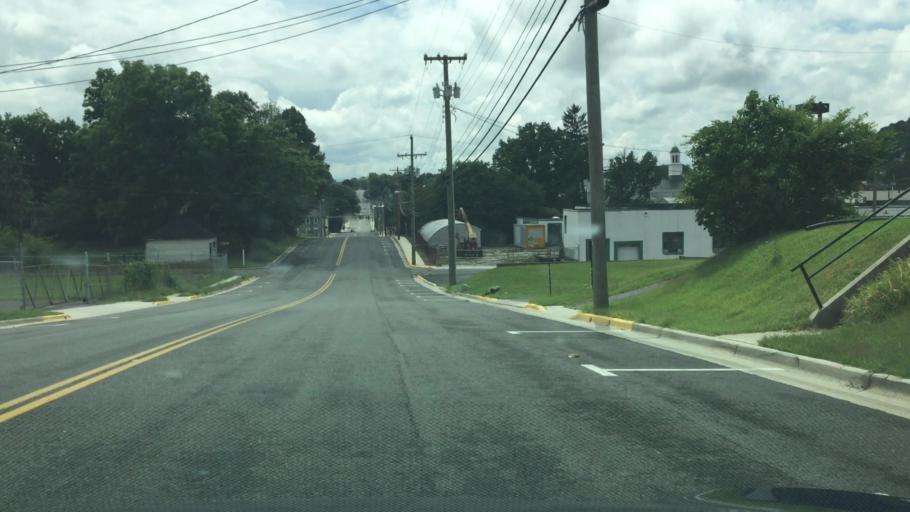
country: US
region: Virginia
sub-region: Wythe County
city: Wytheville
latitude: 36.9518
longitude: -81.0793
